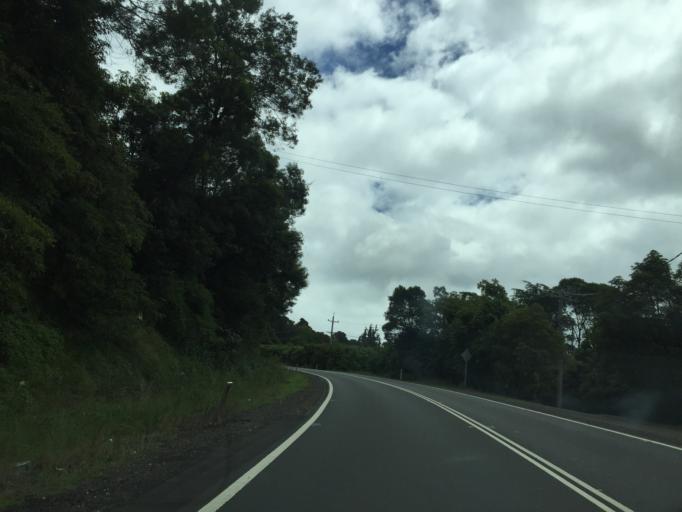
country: AU
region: New South Wales
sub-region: Hawkesbury
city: Richmond
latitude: -33.5253
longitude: 150.6293
